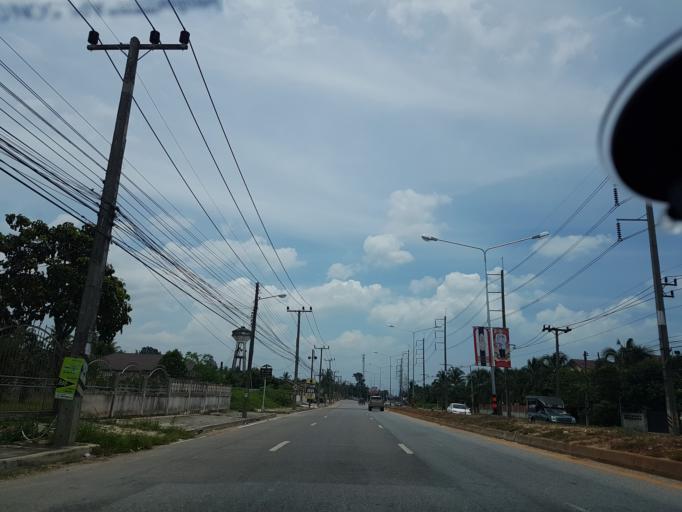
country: TH
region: Songkhla
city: Songkhla
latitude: 7.1133
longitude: 100.6328
